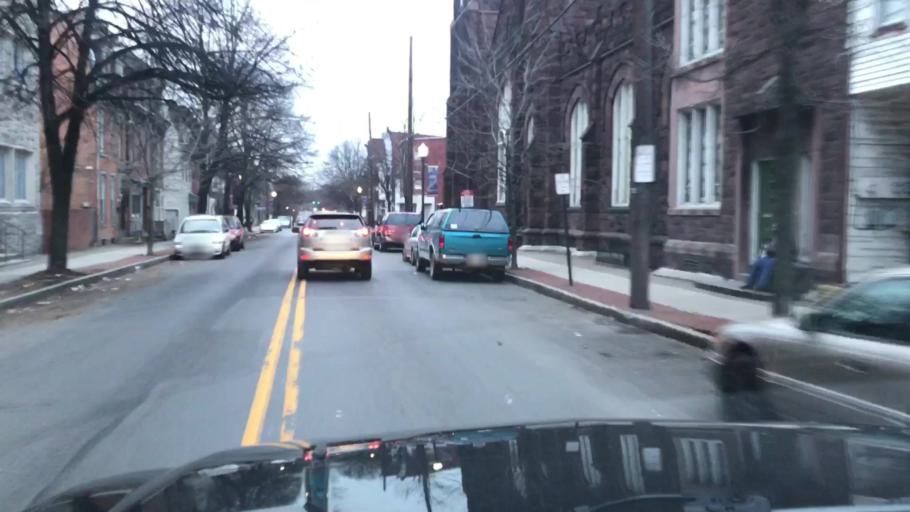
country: US
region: Pennsylvania
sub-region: Dauphin County
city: Harrisburg
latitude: 40.2638
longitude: -76.8691
